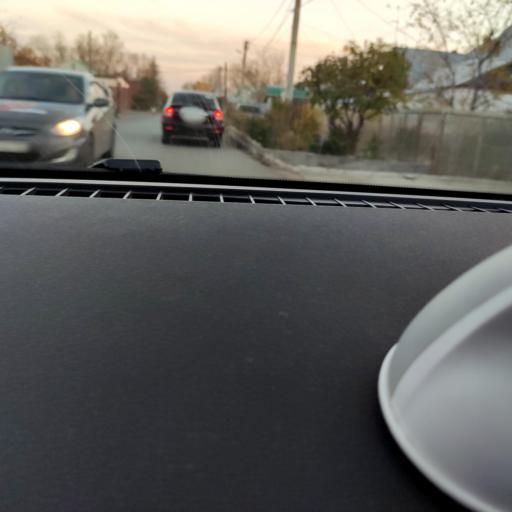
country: RU
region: Samara
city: Samara
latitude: 53.2324
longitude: 50.2355
